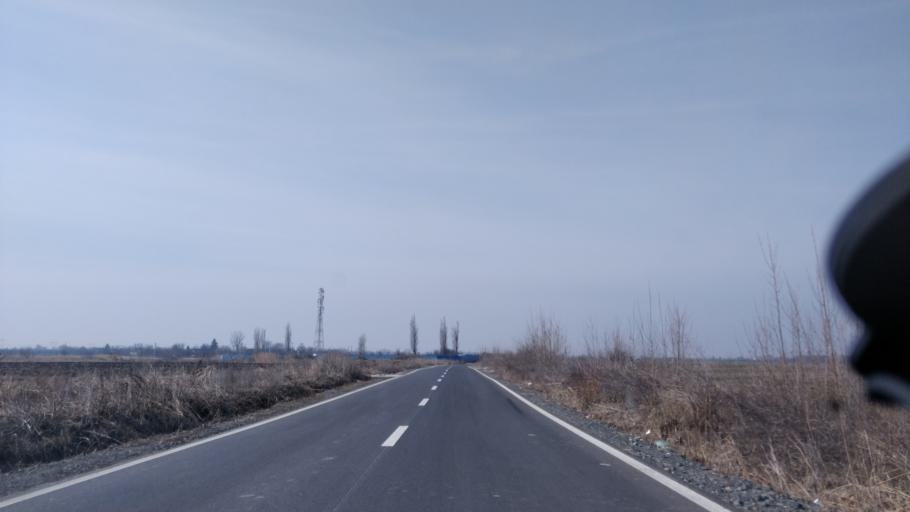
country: RO
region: Giurgiu
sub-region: Comuna Bolintin Deal
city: Bolintin Deal
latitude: 44.4633
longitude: 25.7971
